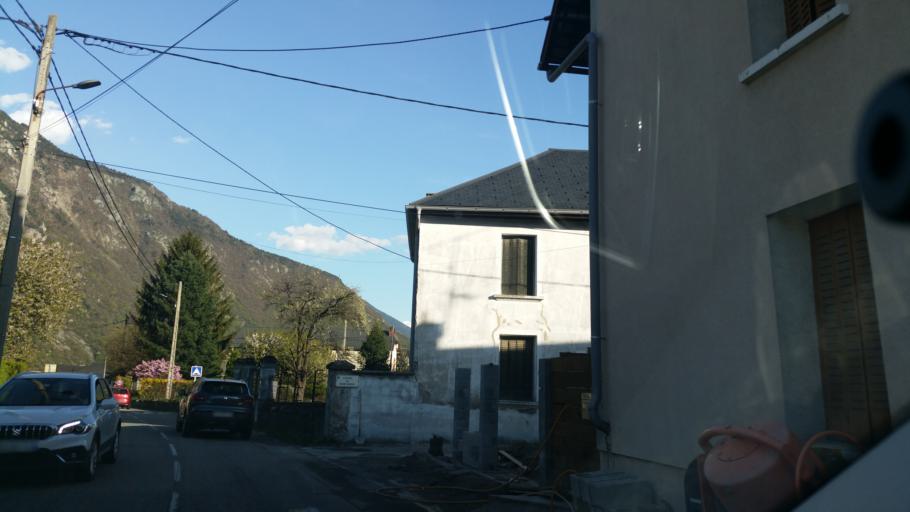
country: FR
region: Rhone-Alpes
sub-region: Departement de la Savoie
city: Saint-Etienne-de-Cuines
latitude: 45.3405
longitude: 6.2986
